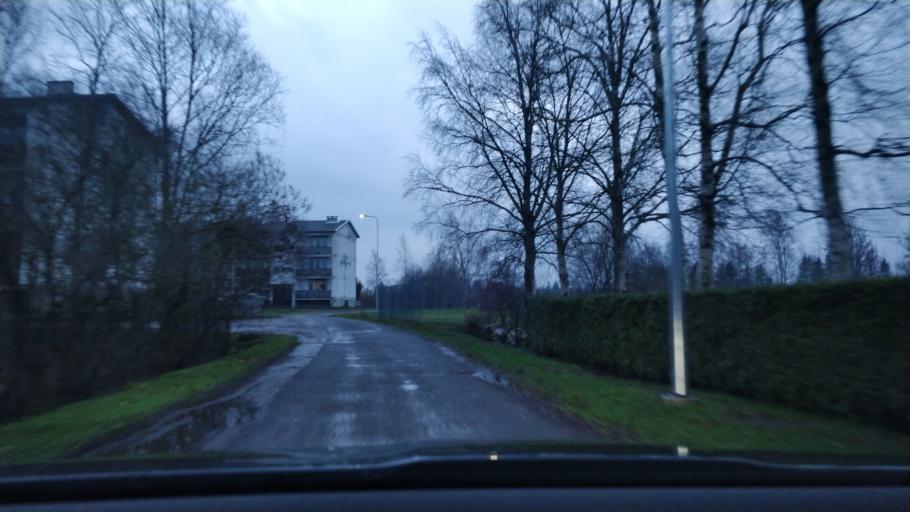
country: EE
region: Laeaene
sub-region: Lihula vald
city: Lihula
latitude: 58.6881
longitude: 23.8377
